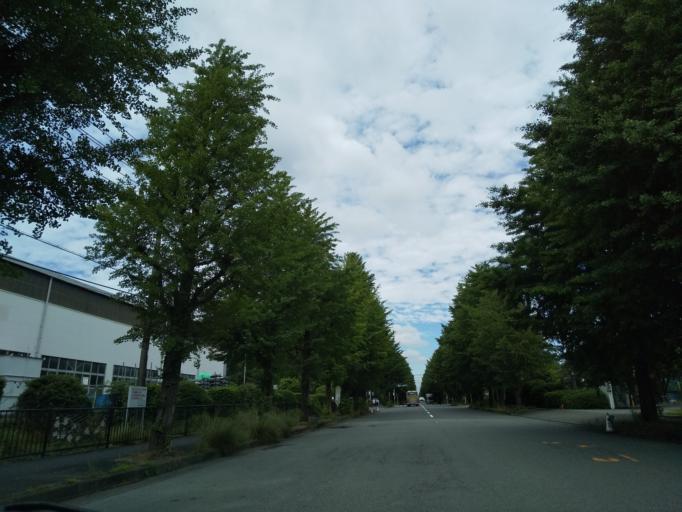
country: JP
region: Kanagawa
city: Zama
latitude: 35.5129
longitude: 139.3493
